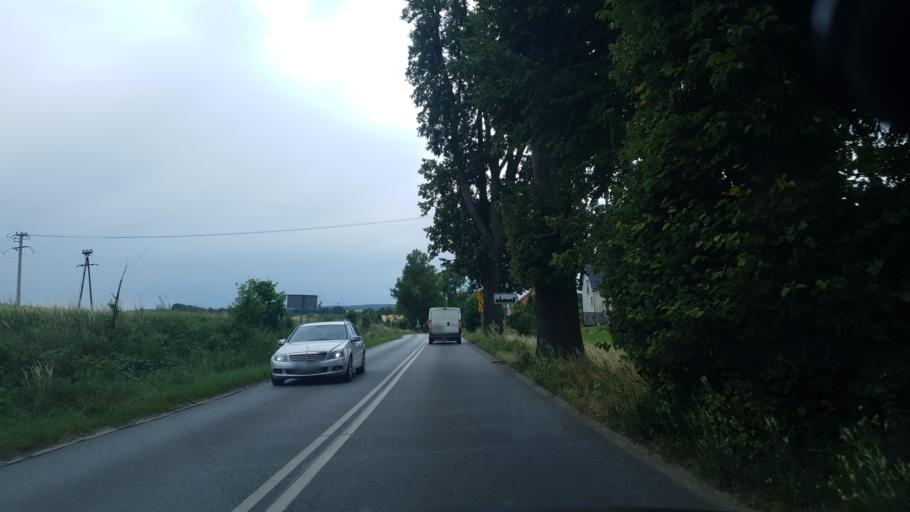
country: PL
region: Pomeranian Voivodeship
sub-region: Powiat kartuski
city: Przodkowo
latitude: 54.3817
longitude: 18.3192
